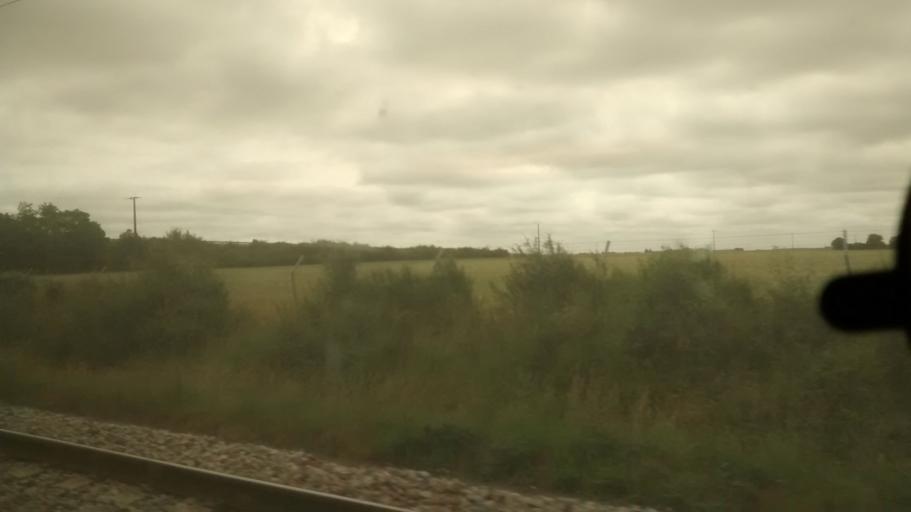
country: FR
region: Centre
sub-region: Departement d'Eure-et-Loir
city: Beville-le-Comte
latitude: 48.4097
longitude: 1.7483
